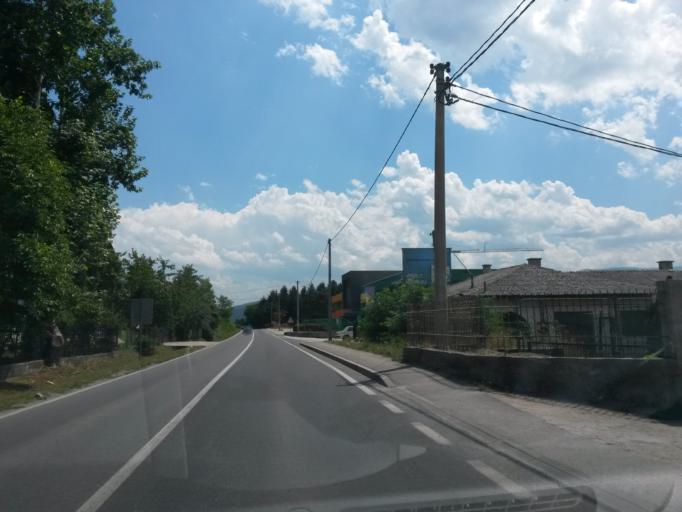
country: BA
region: Federation of Bosnia and Herzegovina
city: Travnik
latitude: 44.2175
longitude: 17.6944
